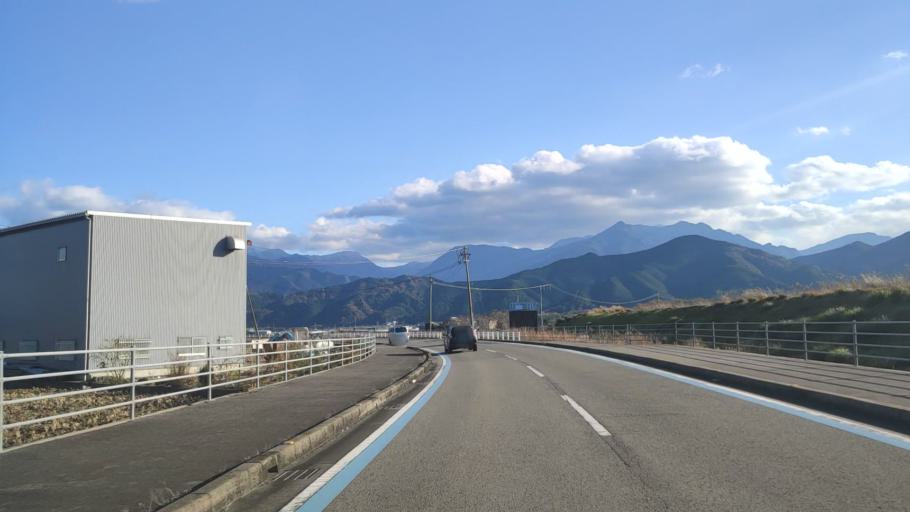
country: JP
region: Ehime
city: Saijo
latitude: 33.9080
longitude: 133.1427
